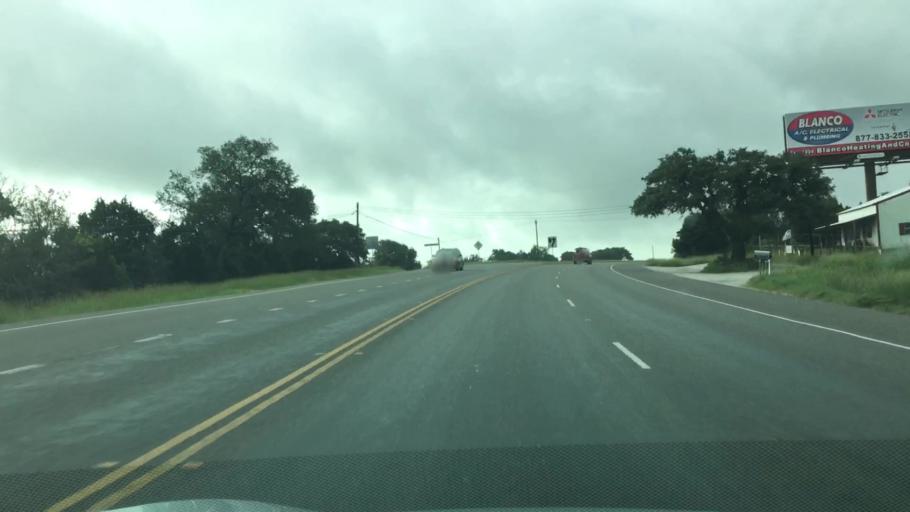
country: US
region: Texas
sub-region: Blanco County
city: Blanco
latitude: 30.0743
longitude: -98.4113
